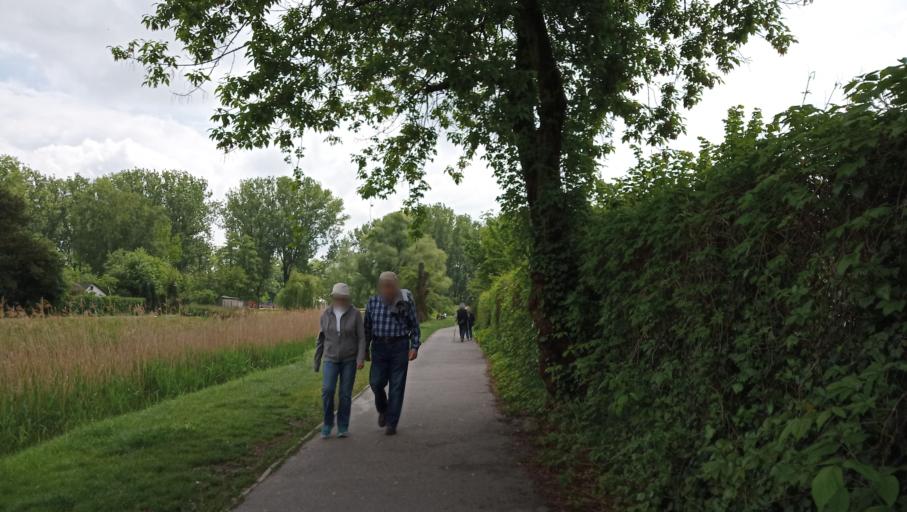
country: PL
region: Masovian Voivodeship
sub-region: Warszawa
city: Zoliborz
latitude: 52.2808
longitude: 20.9874
